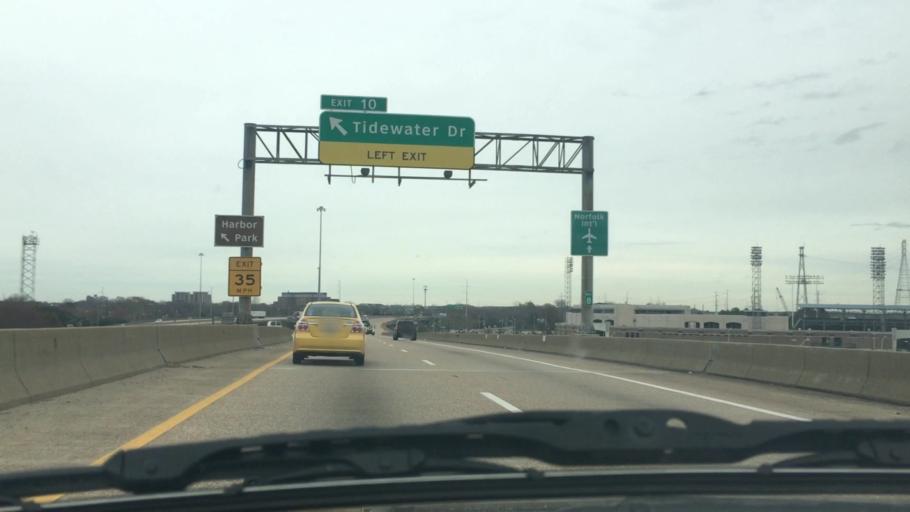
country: US
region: Virginia
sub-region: City of Norfolk
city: Norfolk
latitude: 36.8433
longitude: -76.2832
